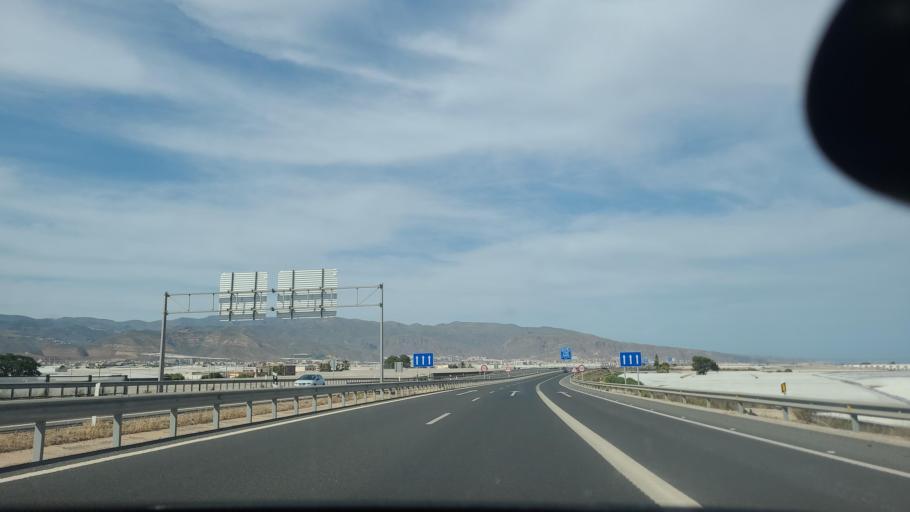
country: ES
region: Andalusia
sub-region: Provincia de Almeria
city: Roquetas de Mar
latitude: 36.7790
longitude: -2.6339
